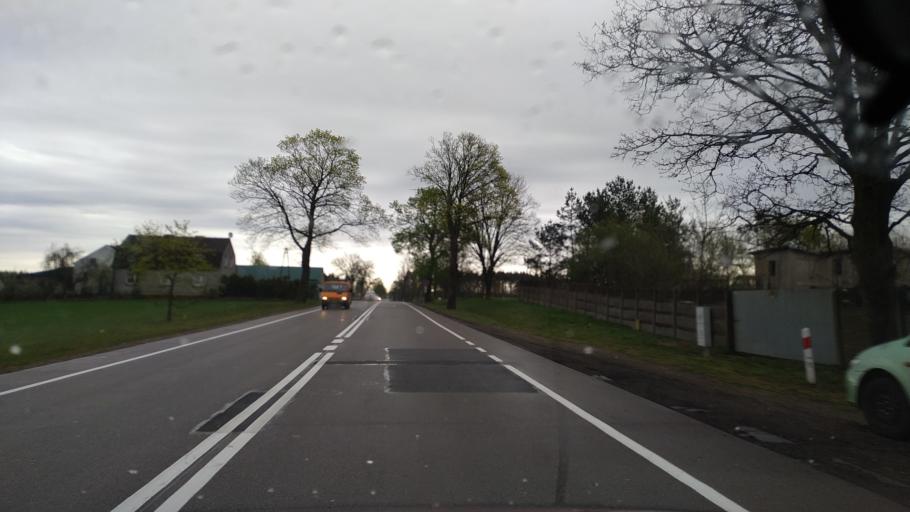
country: PL
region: Pomeranian Voivodeship
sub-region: Powiat chojnicki
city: Czersk
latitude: 53.8063
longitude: 18.0177
